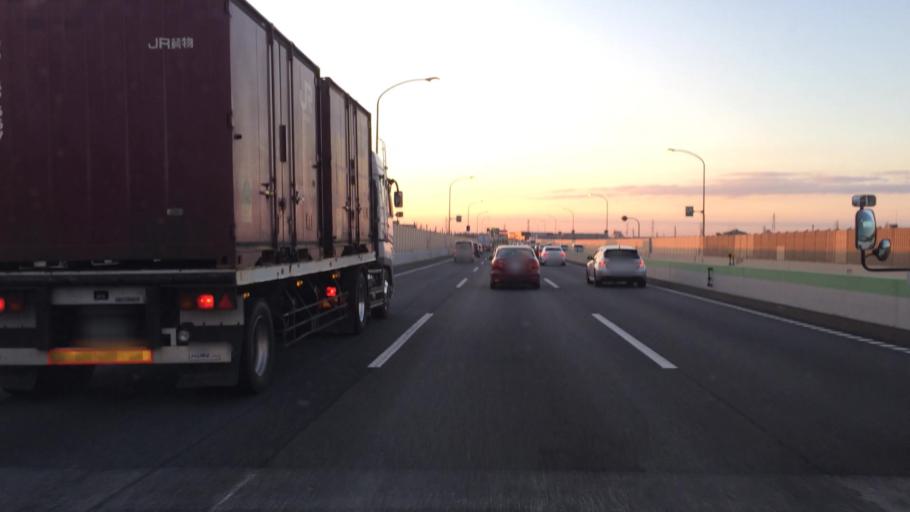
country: JP
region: Chiba
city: Funabashi
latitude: 35.6877
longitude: 139.9797
